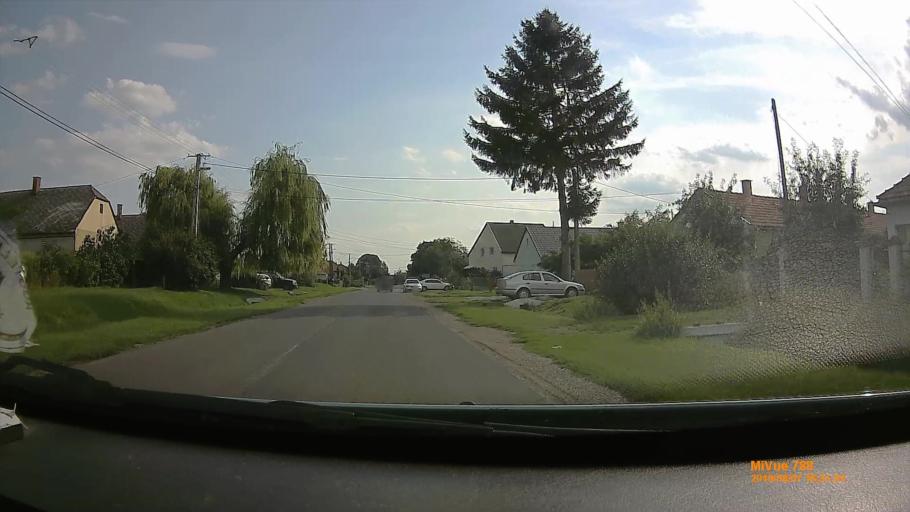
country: HU
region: Borsod-Abauj-Zemplen
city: Gonc
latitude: 48.4233
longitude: 21.2356
